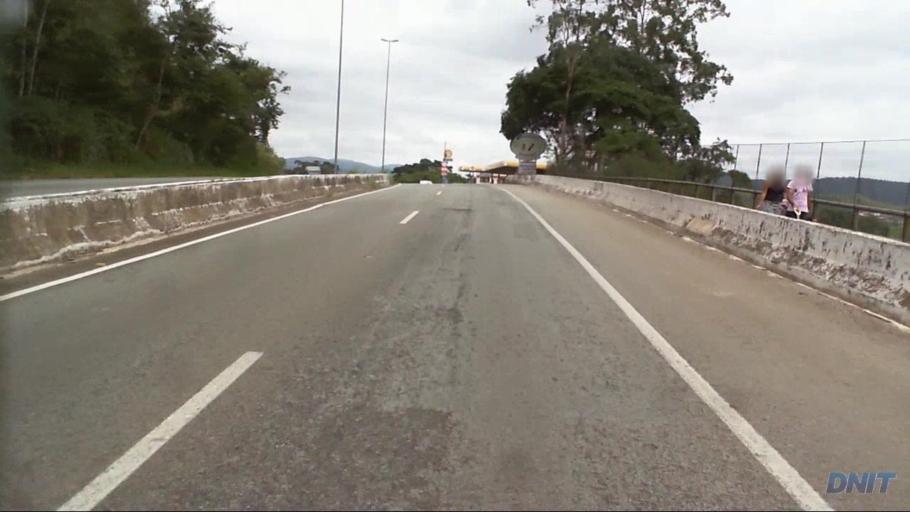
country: BR
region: Minas Gerais
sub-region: Nova Era
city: Nova Era
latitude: -19.7624
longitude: -43.0409
